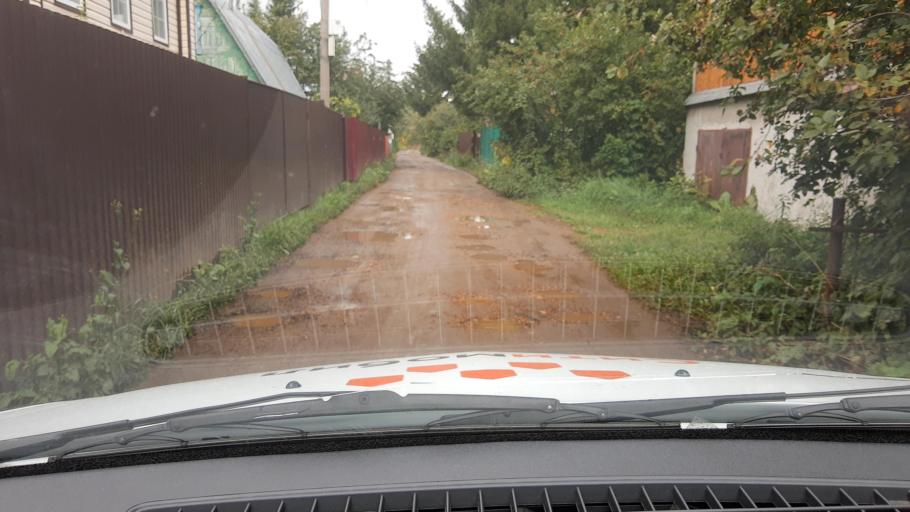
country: RU
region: Bashkortostan
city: Iglino
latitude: 54.7770
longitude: 56.2008
